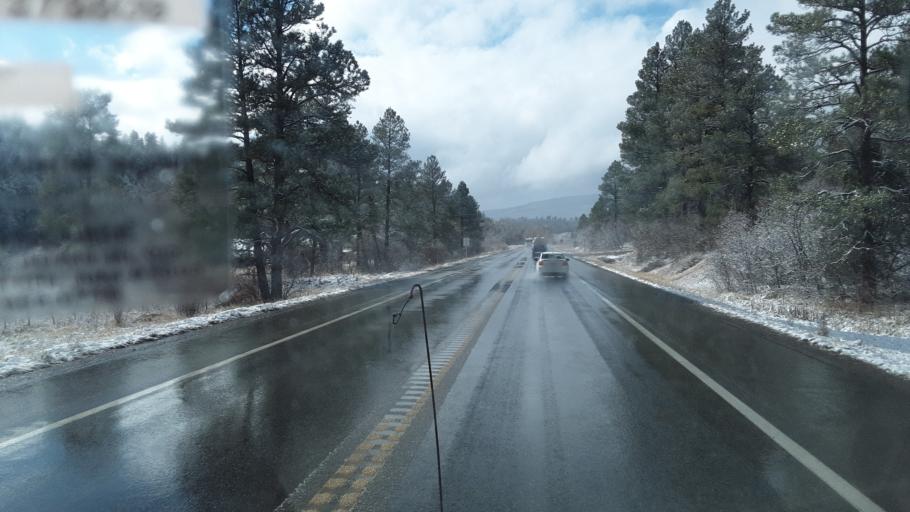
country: US
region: Colorado
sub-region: Archuleta County
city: Pagosa Springs
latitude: 37.2383
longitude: -107.1337
